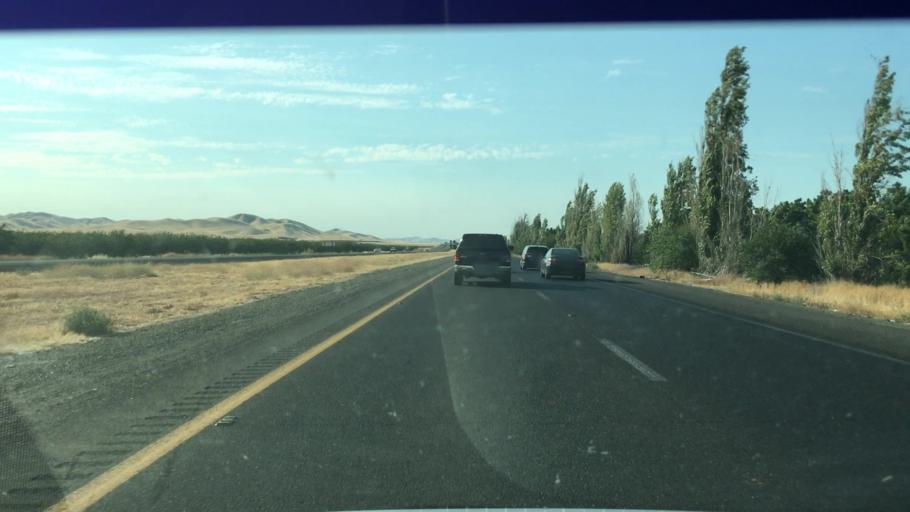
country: US
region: California
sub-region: Merced County
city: Gustine
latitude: 37.1369
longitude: -121.0366
